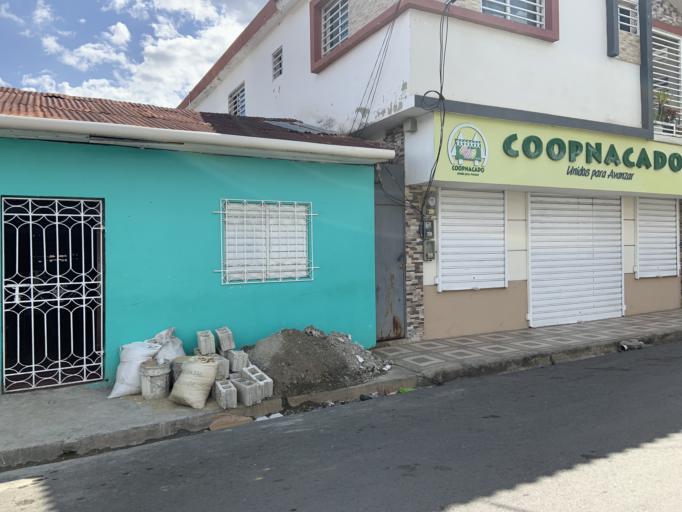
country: DO
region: Monte Plata
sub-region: Yamasa
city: Yamasa
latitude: 18.7686
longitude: -70.0247
